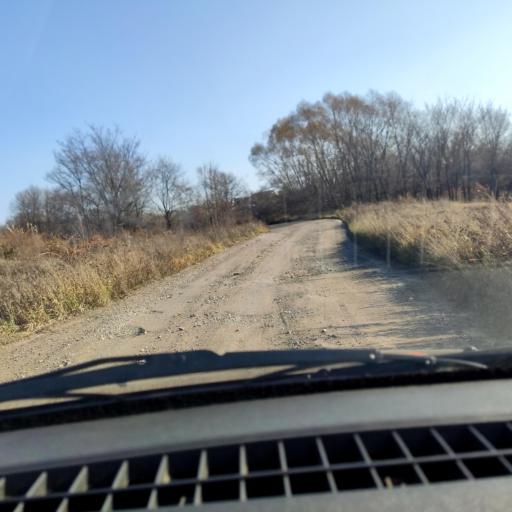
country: RU
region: Bashkortostan
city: Avdon
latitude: 54.4905
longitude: 55.8478
